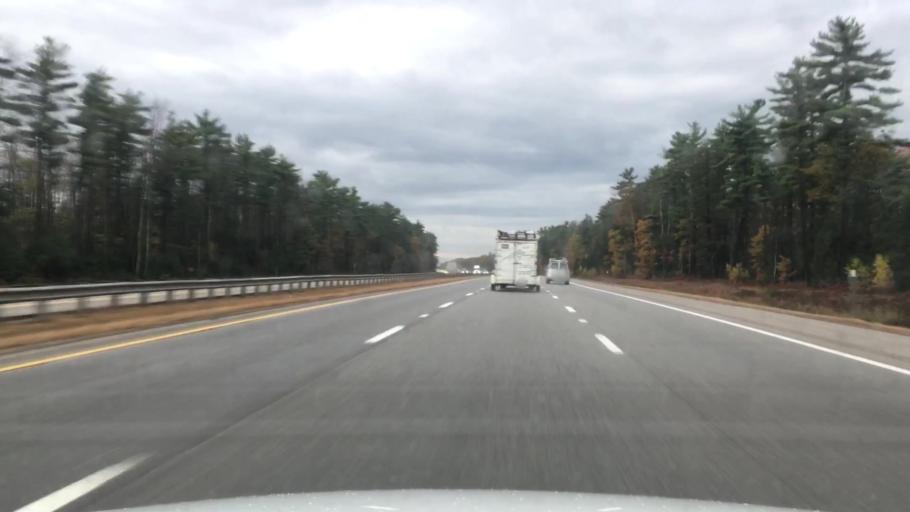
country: US
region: Maine
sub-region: York County
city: West Kennebunk
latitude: 43.4274
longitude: -70.5496
